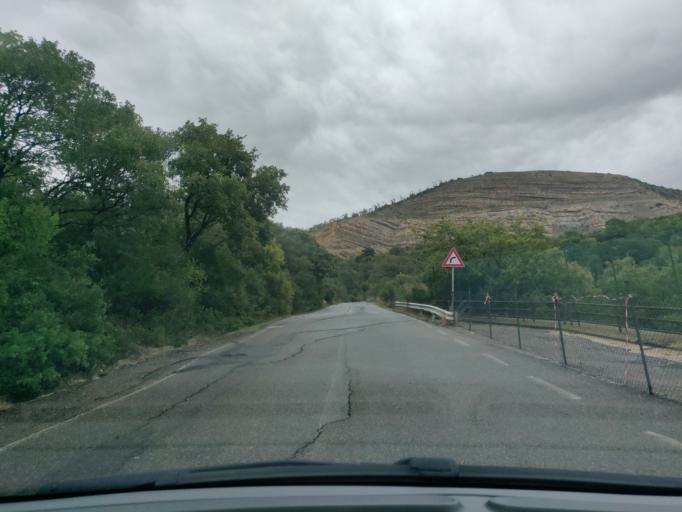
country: IT
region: Latium
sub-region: Citta metropolitana di Roma Capitale
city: Allumiere
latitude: 42.1290
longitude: 11.8536
